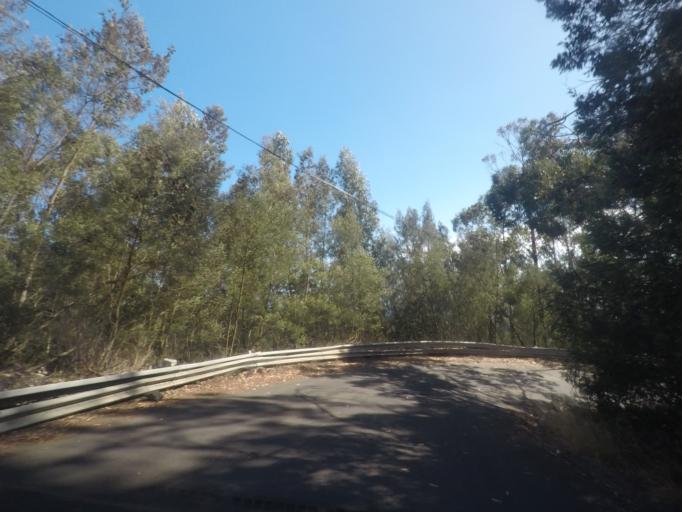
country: PT
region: Madeira
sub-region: Ribeira Brava
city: Campanario
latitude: 32.6838
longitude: -17.0228
